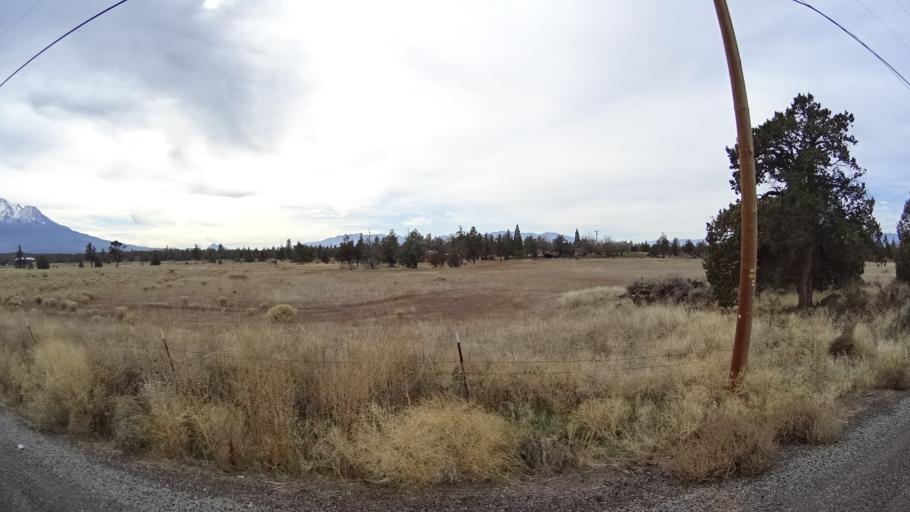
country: US
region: California
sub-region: Siskiyou County
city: Weed
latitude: 41.5981
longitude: -122.3432
